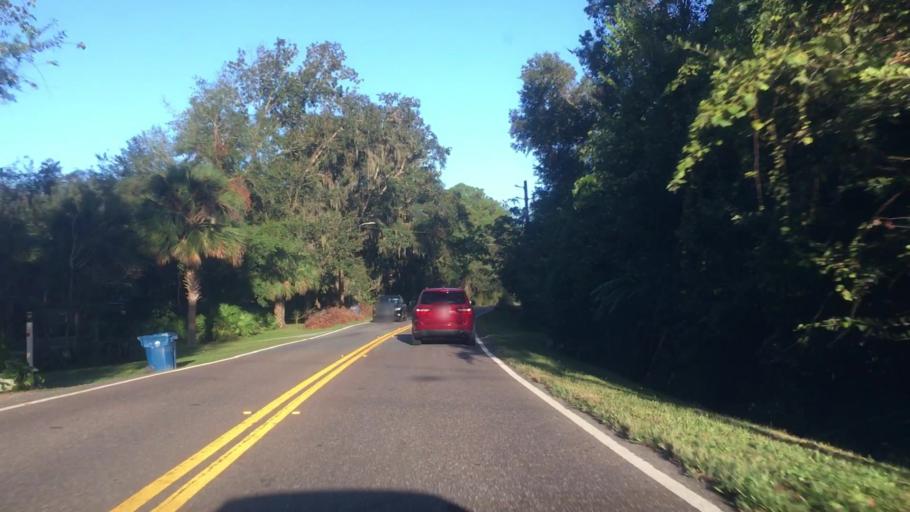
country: US
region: Florida
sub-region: Duval County
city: Jacksonville
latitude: 30.4651
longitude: -81.5951
